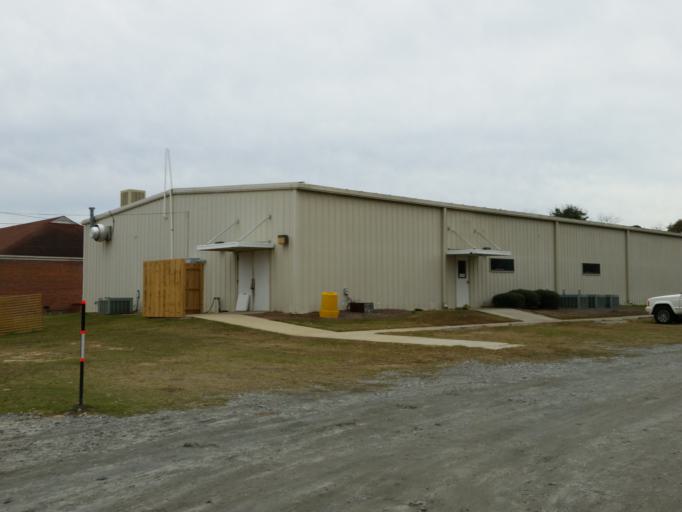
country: US
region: Georgia
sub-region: Dooly County
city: Unadilla
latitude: 32.1920
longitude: -83.7630
